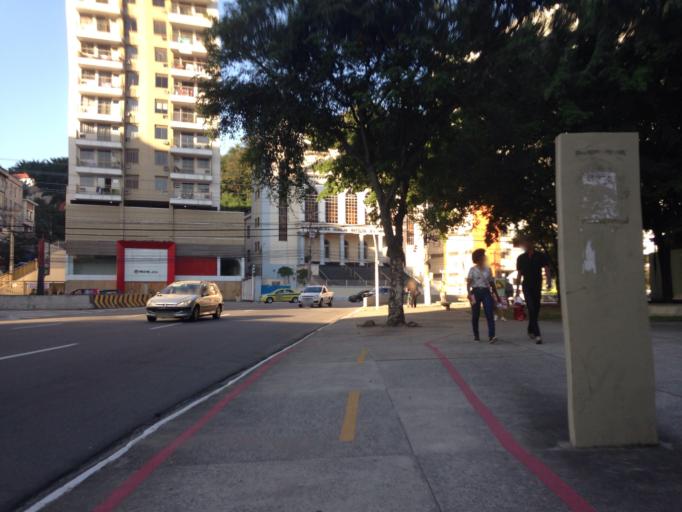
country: BR
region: Rio de Janeiro
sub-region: Niteroi
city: Niteroi
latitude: -22.8939
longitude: -43.1140
